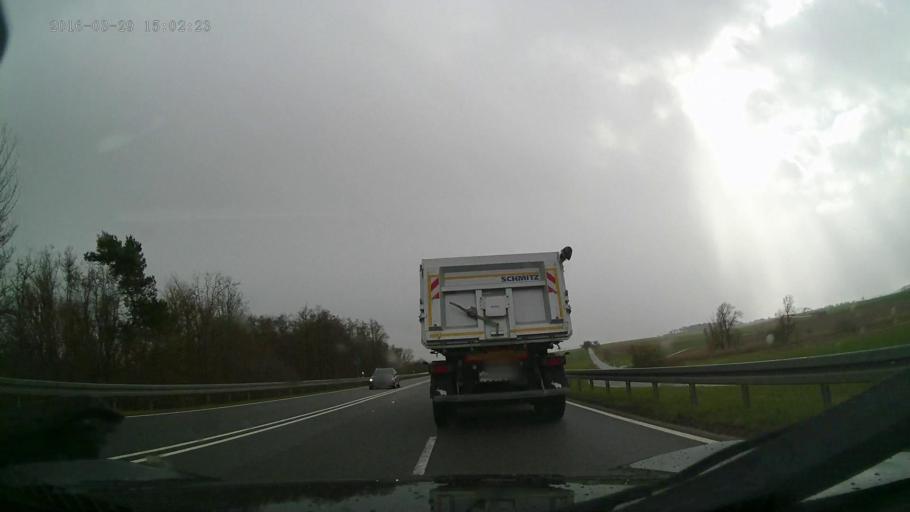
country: DE
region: Baden-Wuerttemberg
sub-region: Karlsruhe Region
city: Walldurn
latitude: 49.5606
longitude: 9.3603
